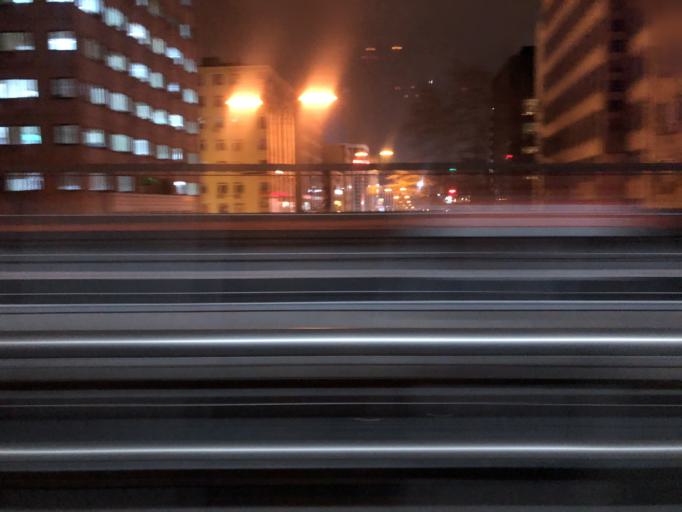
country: TR
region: Ankara
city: Ankara
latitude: 39.9213
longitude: 32.8583
